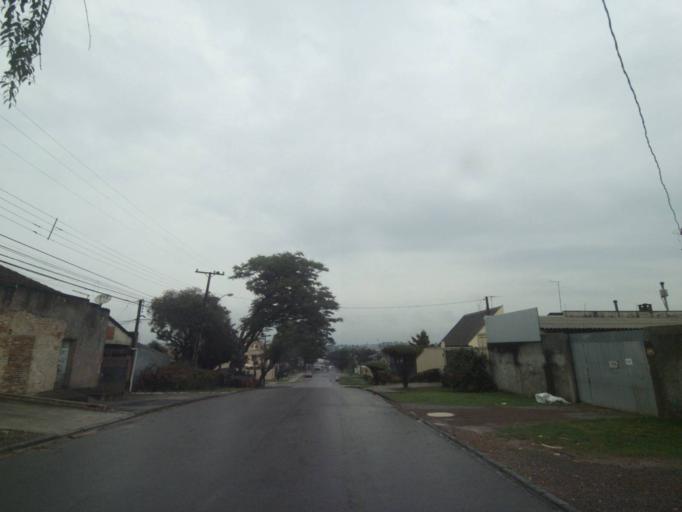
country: BR
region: Parana
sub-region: Curitiba
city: Curitiba
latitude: -25.4818
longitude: -49.3096
